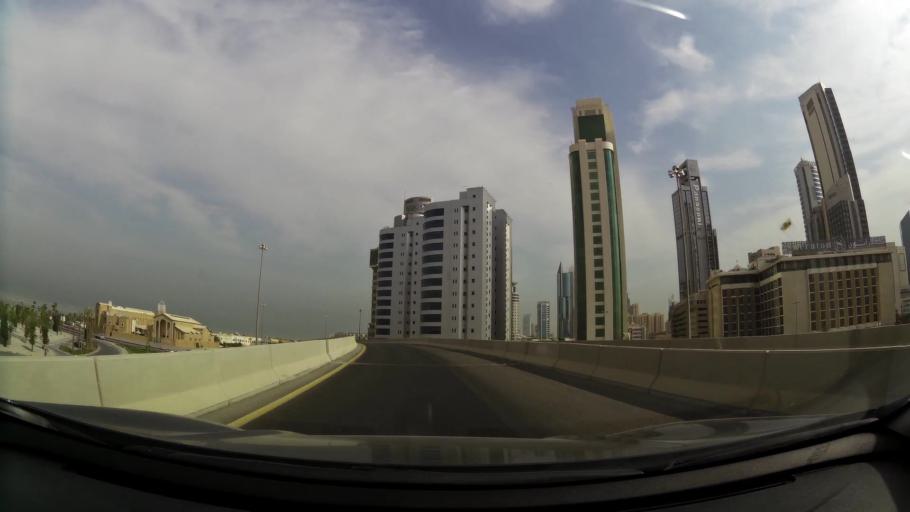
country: KW
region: Al Asimah
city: Ash Shamiyah
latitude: 29.3616
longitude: 47.9606
